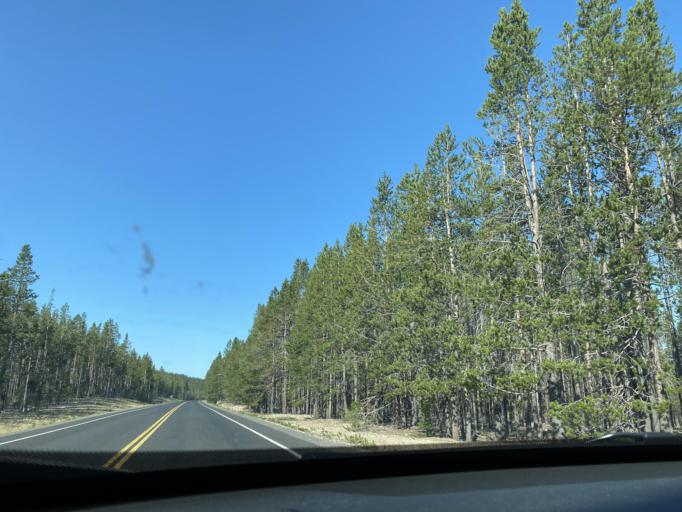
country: US
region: Oregon
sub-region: Deschutes County
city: Three Rivers
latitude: 43.7066
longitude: -121.2409
